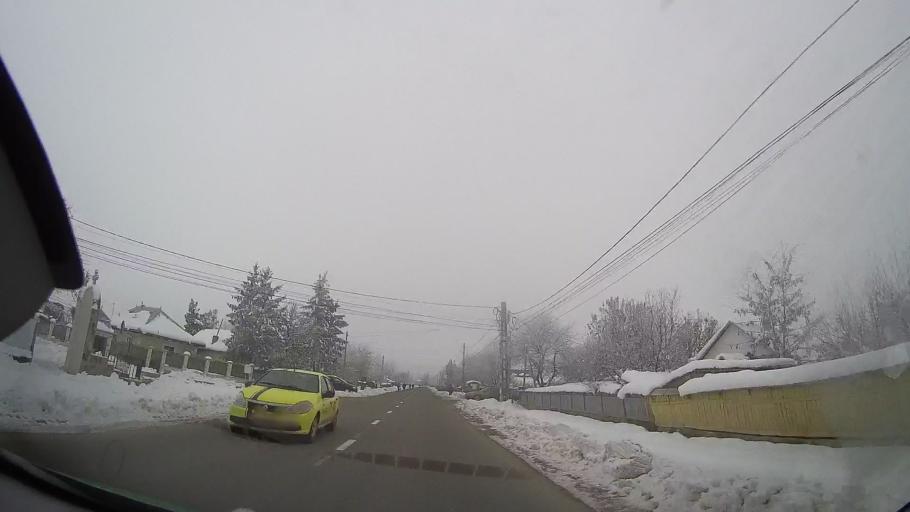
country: RO
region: Neamt
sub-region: Comuna Horia
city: Cotu Vames
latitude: 46.9010
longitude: 26.9552
